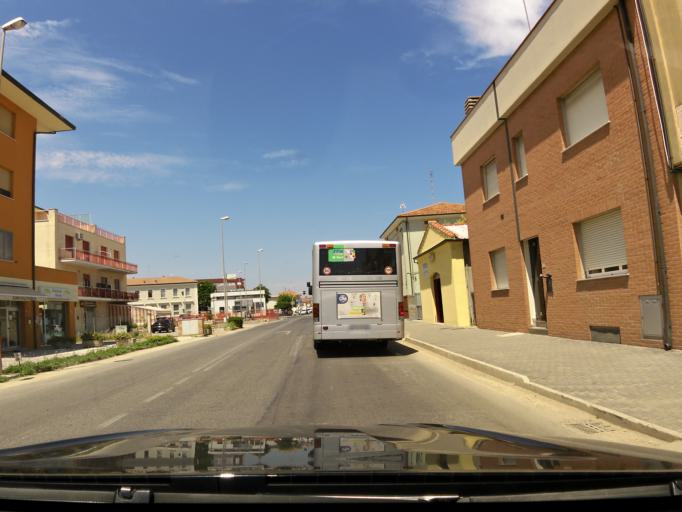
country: IT
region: The Marches
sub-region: Provincia di Pesaro e Urbino
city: Marotta
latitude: 43.7672
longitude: 13.1410
